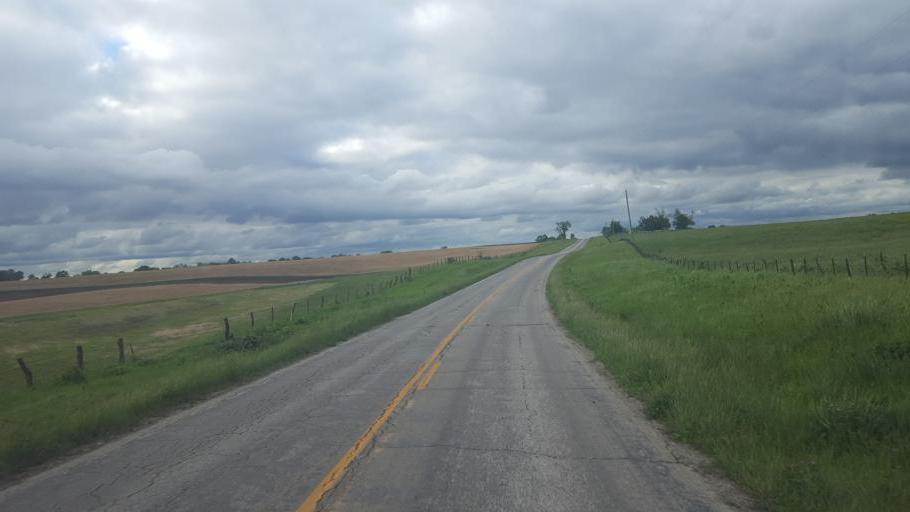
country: US
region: Missouri
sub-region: Mercer County
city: Princeton
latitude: 40.2840
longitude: -93.6802
